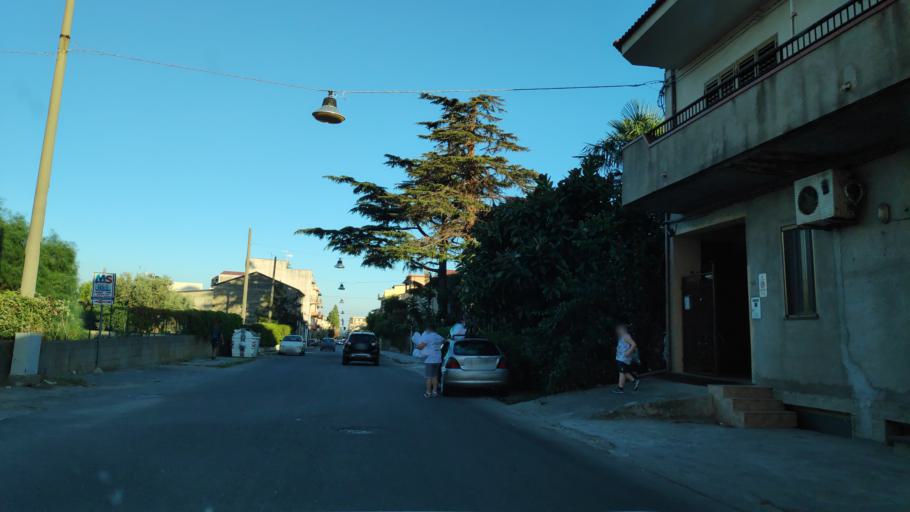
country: IT
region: Calabria
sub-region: Provincia di Reggio Calabria
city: Locri
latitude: 38.2380
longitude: 16.2568
